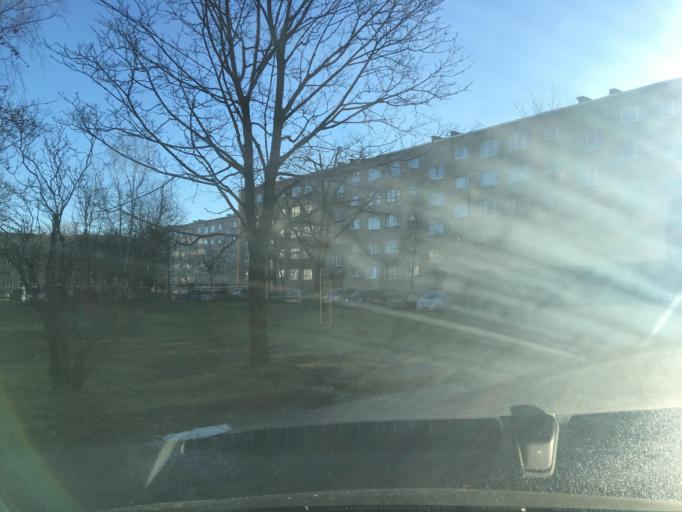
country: EE
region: Ida-Virumaa
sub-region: Narva linn
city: Narva
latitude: 59.3836
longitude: 28.1749
